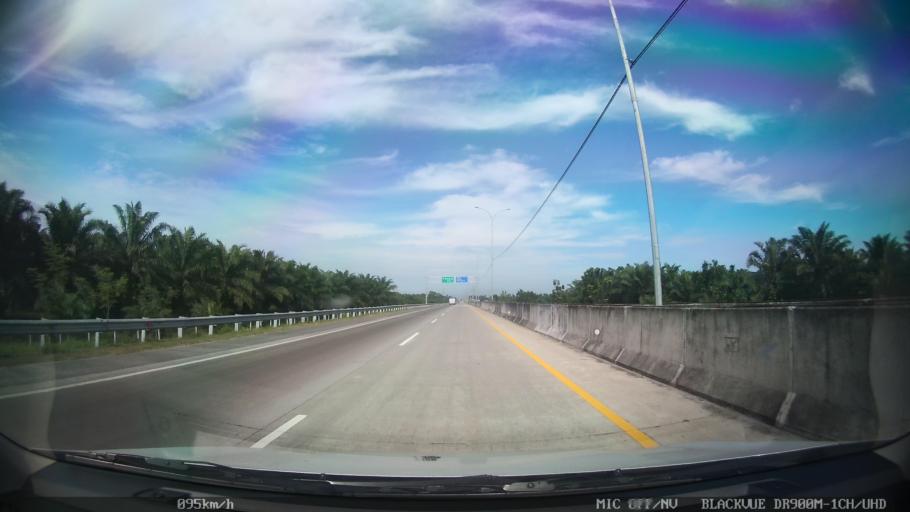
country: ID
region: North Sumatra
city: Sunggal
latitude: 3.6382
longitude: 98.6033
